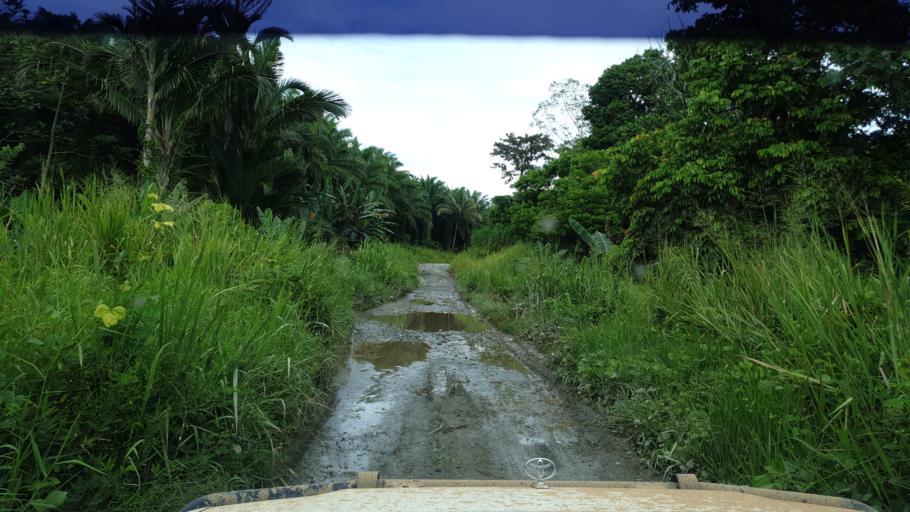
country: PG
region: Northern Province
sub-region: Sohe
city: Kokoda
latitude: -8.9172
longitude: 147.8612
